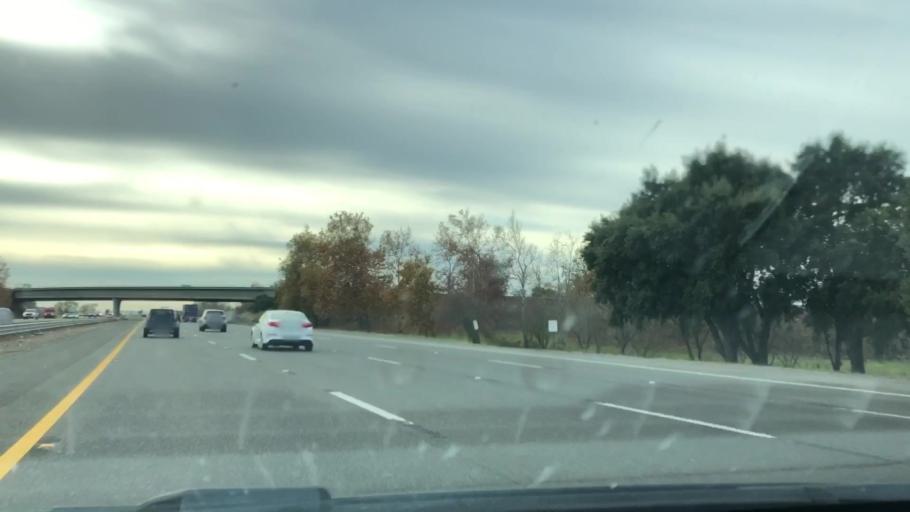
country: US
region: California
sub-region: Yolo County
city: Davis
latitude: 38.5231
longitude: -121.7673
